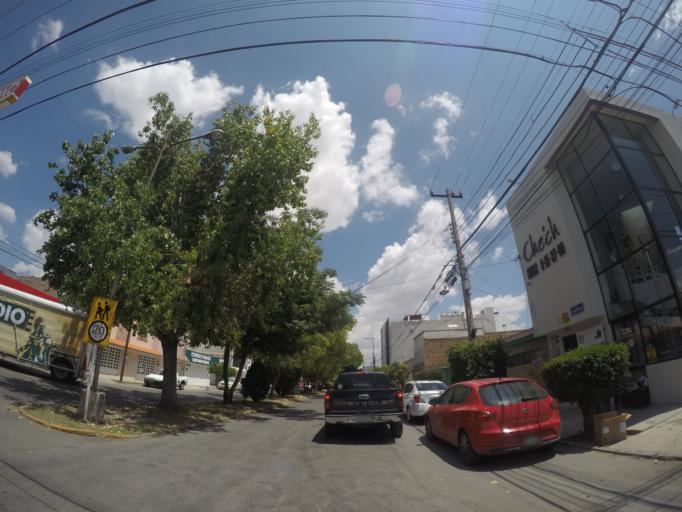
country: MX
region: San Luis Potosi
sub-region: San Luis Potosi
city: San Luis Potosi
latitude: 22.1437
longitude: -100.9876
